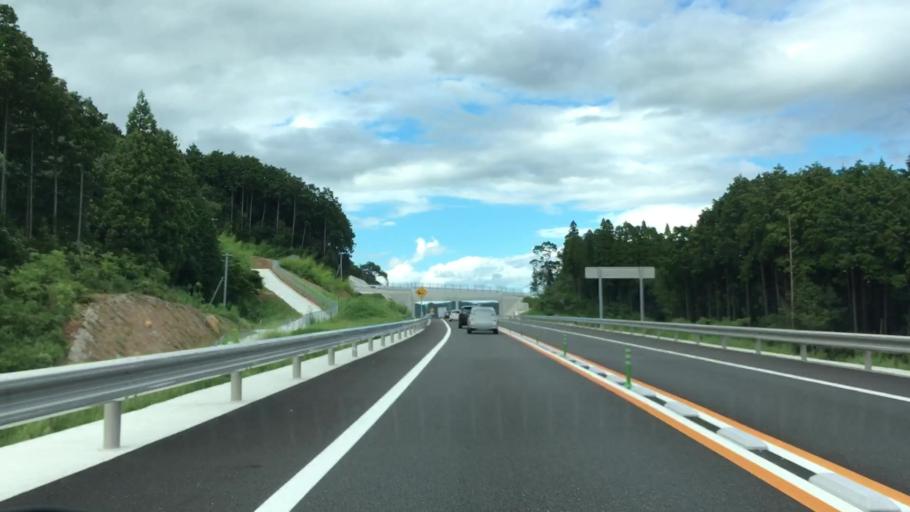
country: JP
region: Saga Prefecture
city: Imaricho-ko
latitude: 33.3297
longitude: 129.9279
